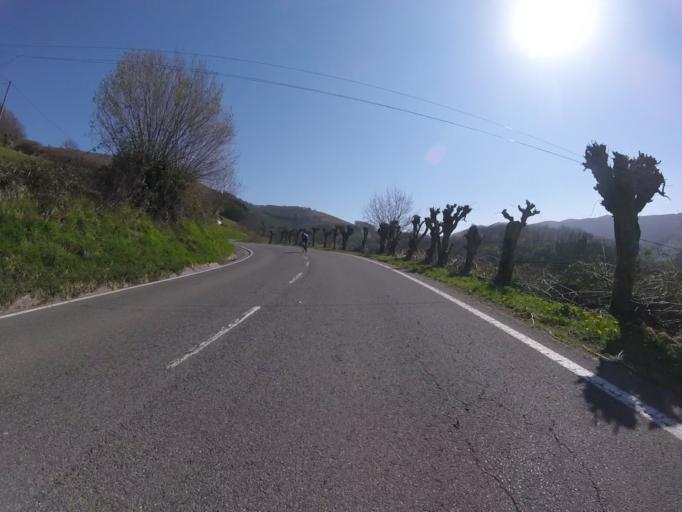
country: ES
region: Navarre
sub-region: Provincia de Navarra
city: Leitza
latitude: 43.0888
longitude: -1.9005
